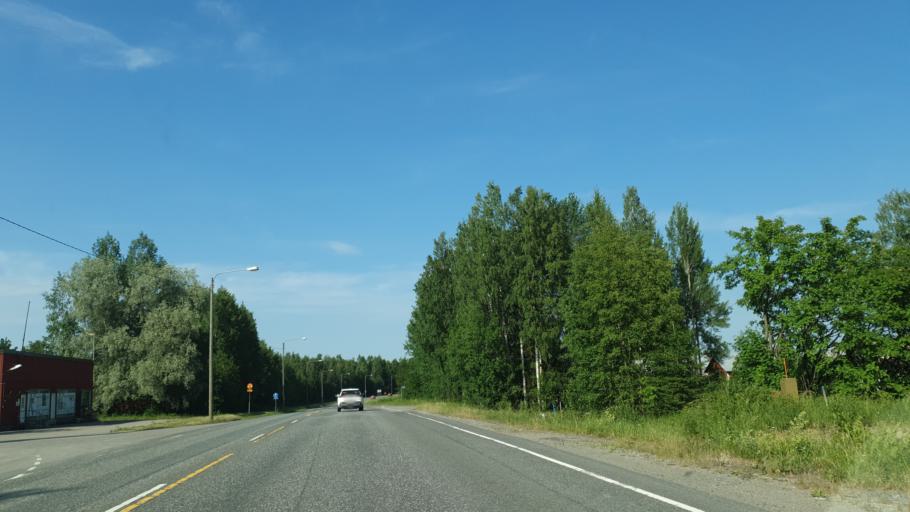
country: FI
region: Northern Savo
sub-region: Kuopio
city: Siilinjaervi
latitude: 63.1274
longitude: 27.7729
